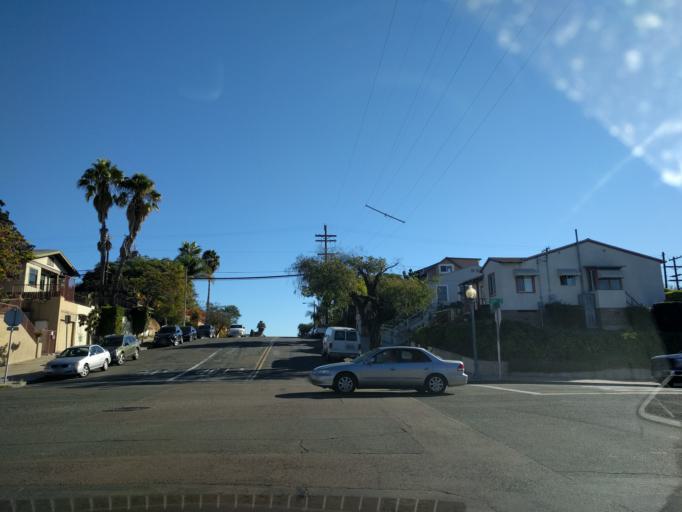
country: US
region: California
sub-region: San Diego County
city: San Diego
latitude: 32.7169
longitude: -117.1339
